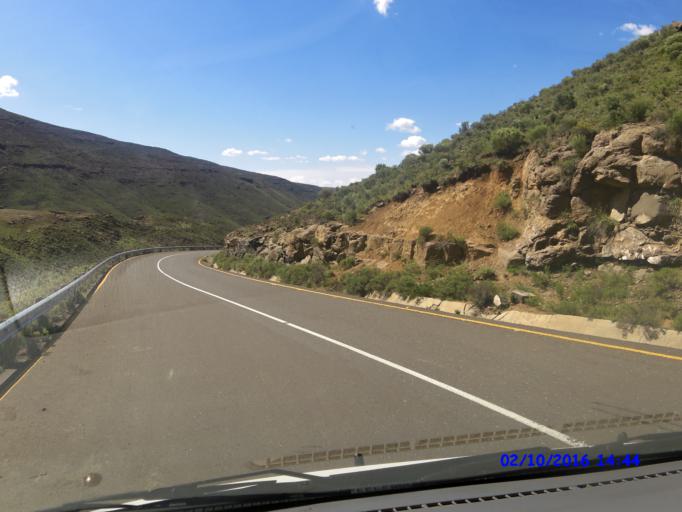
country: LS
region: Maseru
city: Nako
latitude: -29.5245
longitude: 28.0614
